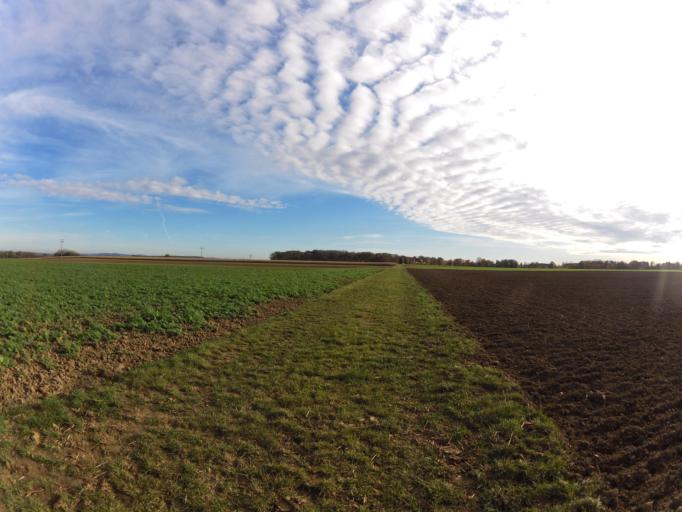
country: DE
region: Bavaria
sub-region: Regierungsbezirk Unterfranken
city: Giebelstadt
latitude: 49.6658
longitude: 9.9746
